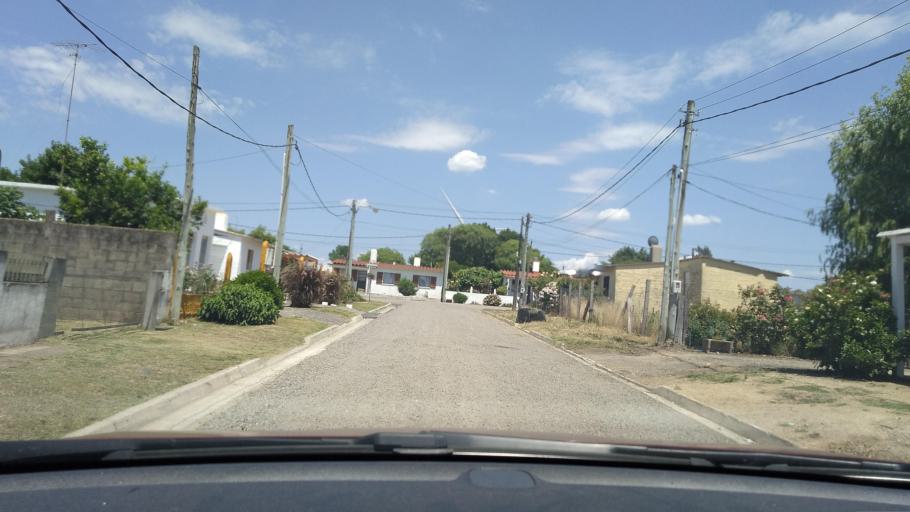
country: UY
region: Canelones
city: Tala
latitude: -34.2049
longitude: -55.7423
